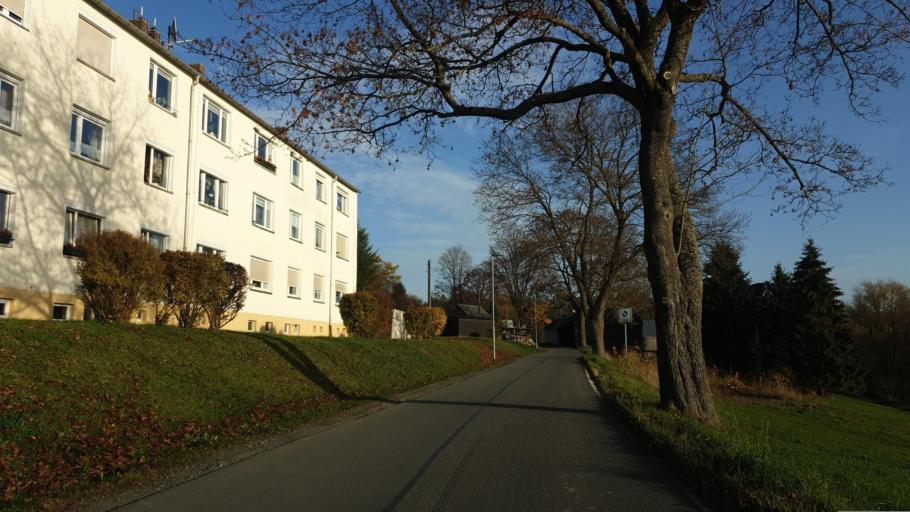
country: DE
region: Saxony
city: Markneukirchen
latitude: 50.2716
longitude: 12.3216
